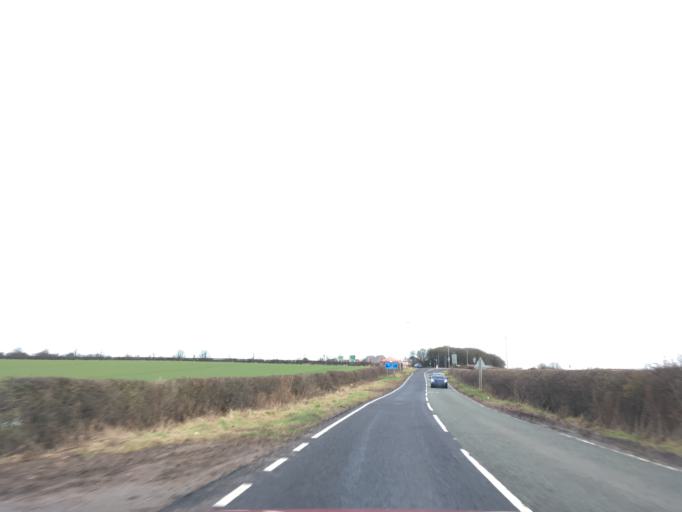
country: GB
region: England
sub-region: Nottinghamshire
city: Ruddington
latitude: 52.8995
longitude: -1.1225
